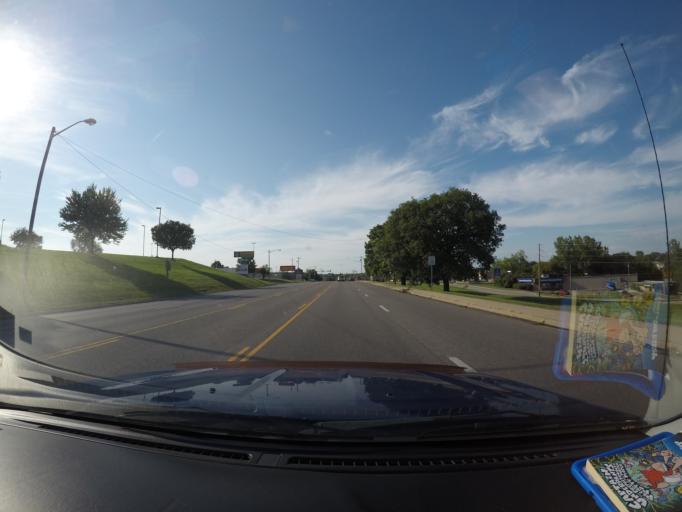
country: US
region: Kansas
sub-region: Leavenworth County
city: Leavenworth
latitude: 39.2834
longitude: -94.9033
